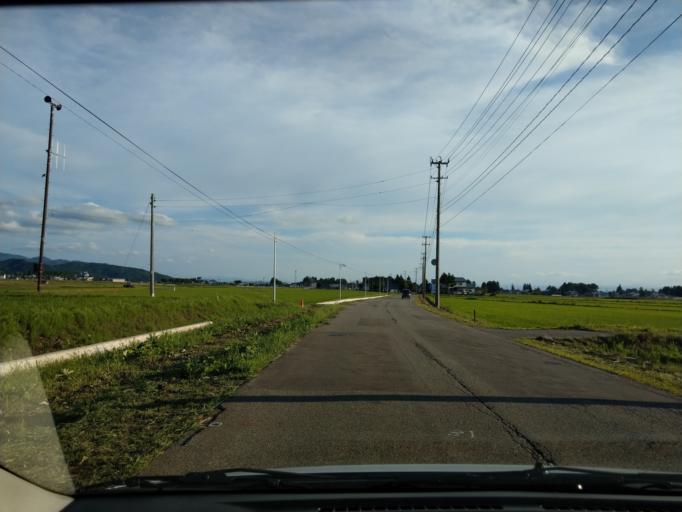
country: JP
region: Akita
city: Kakunodatemachi
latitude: 39.4818
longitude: 140.5896
